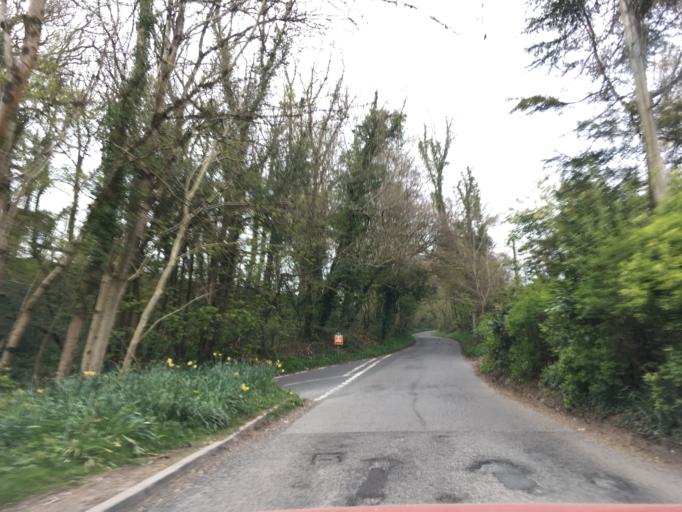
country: GB
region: Wales
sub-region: Caerphilly County Borough
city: Caerphilly
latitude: 51.5497
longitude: -3.2367
